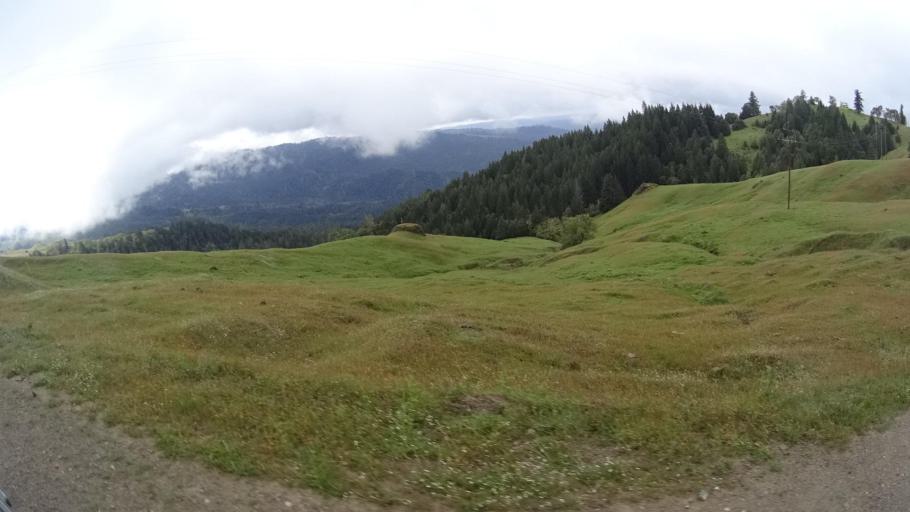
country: US
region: California
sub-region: Humboldt County
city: Redway
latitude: 40.2131
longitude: -123.7407
